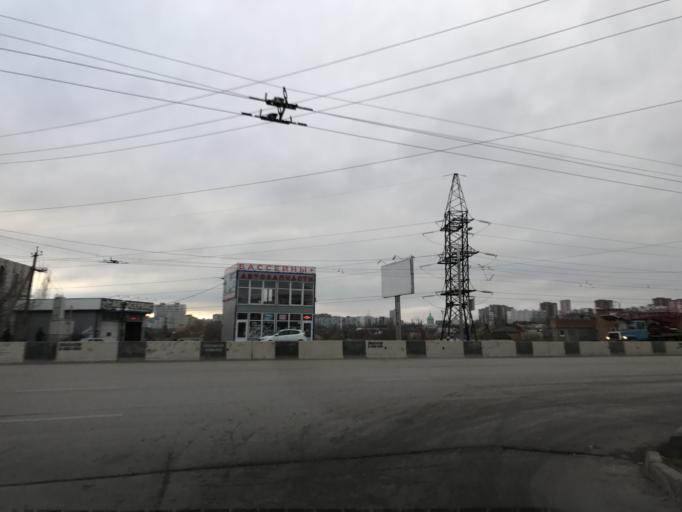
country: RU
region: Rostov
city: Temernik
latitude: 47.2923
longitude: 39.7330
